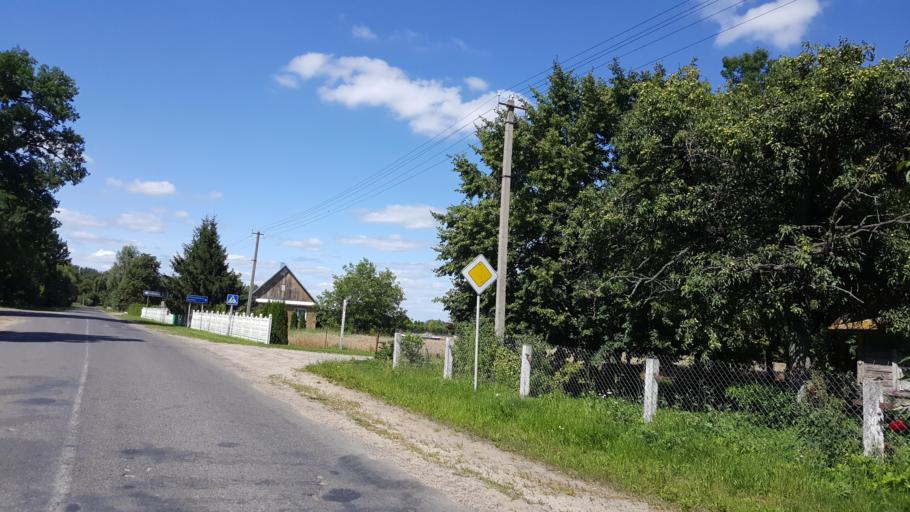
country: BY
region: Brest
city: Horad Kobryn
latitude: 52.2999
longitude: 24.3690
